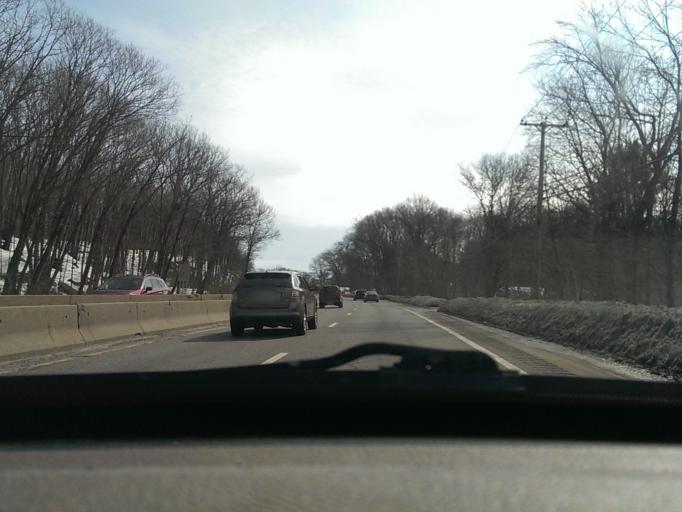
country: US
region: Massachusetts
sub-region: Worcester County
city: Millbury
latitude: 42.1829
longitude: -71.7627
